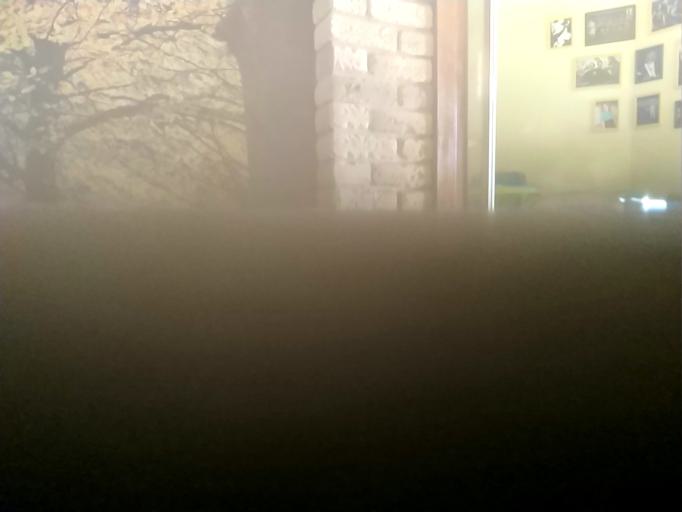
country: RU
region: Kaluga
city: Yukhnov
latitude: 54.8385
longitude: 34.9990
